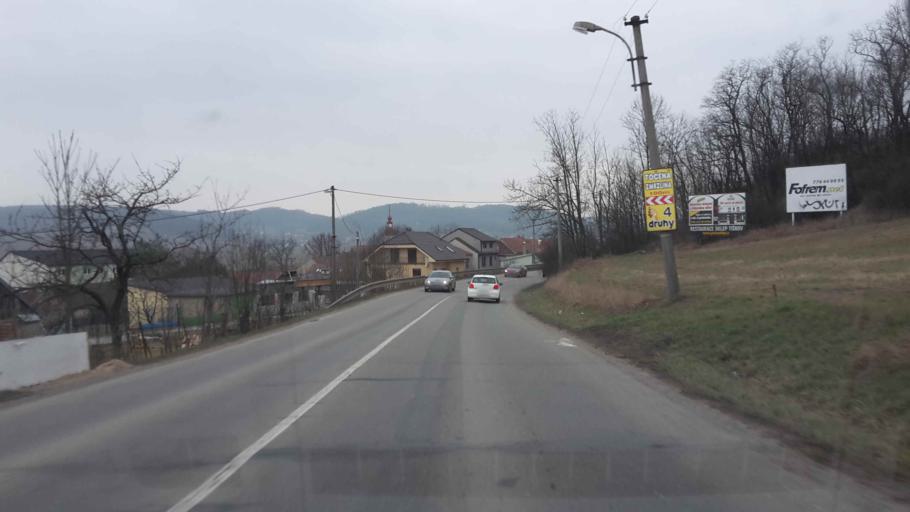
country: CZ
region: South Moravian
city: Cebin
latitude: 49.3131
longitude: 16.4818
